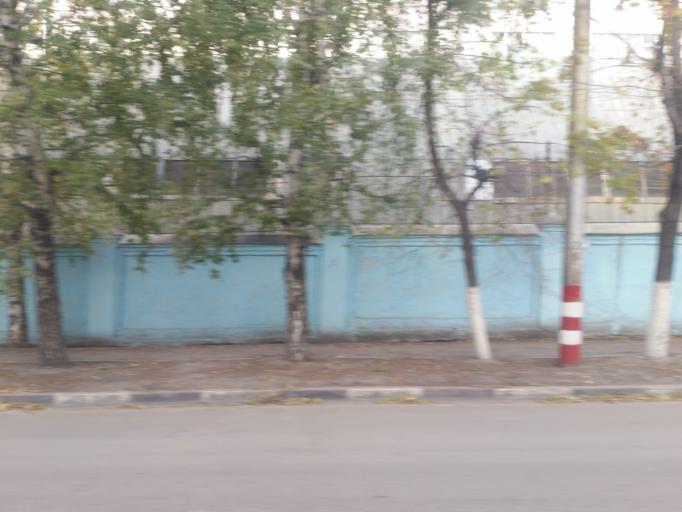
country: RU
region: Ulyanovsk
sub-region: Ulyanovskiy Rayon
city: Ulyanovsk
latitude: 54.3196
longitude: 48.3893
